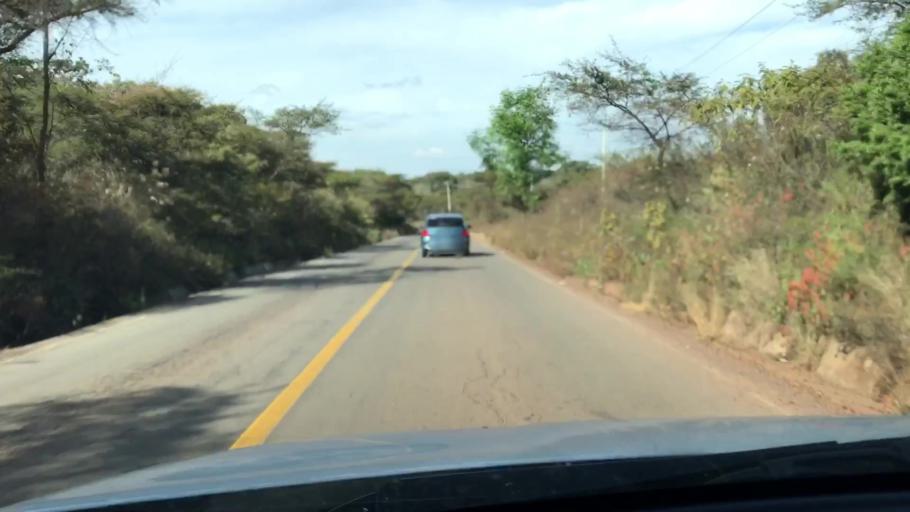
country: MX
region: Jalisco
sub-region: Zacoalco de Torres
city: Barranca de Otates (Barranca de Otatan)
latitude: 20.1967
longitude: -103.6936
